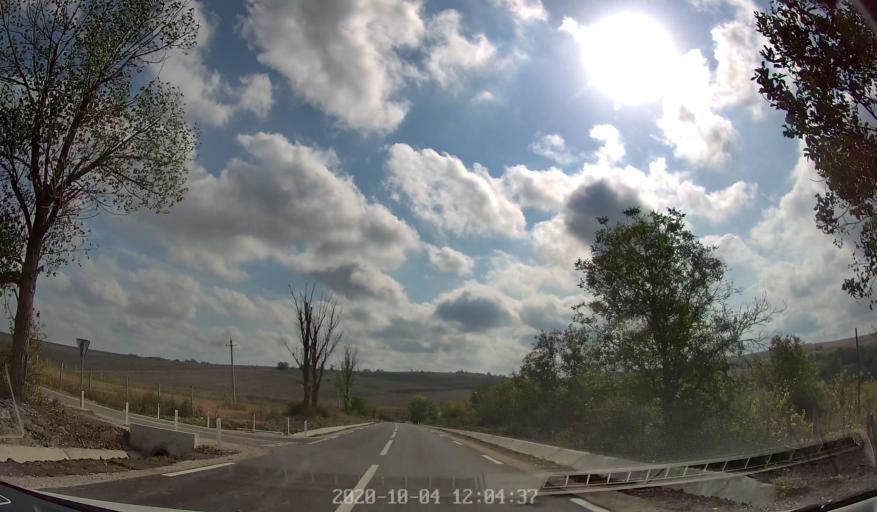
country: MD
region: Rezina
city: Saharna
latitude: 47.6021
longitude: 28.9452
